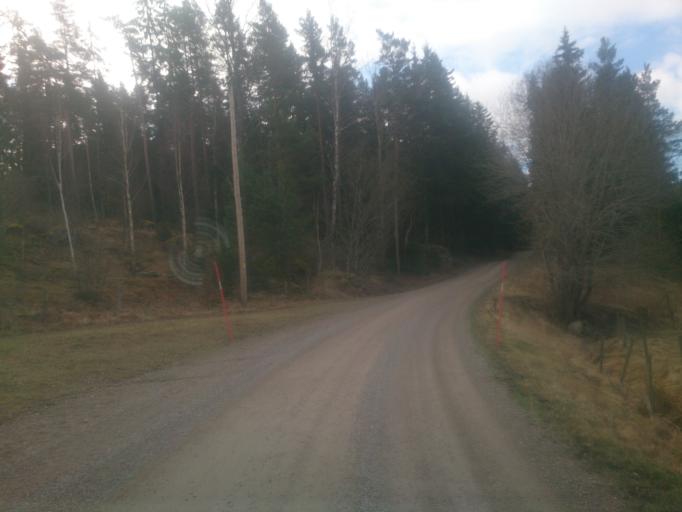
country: SE
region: OEstergoetland
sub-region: Atvidabergs Kommun
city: Atvidaberg
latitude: 58.2186
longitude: 16.1692
